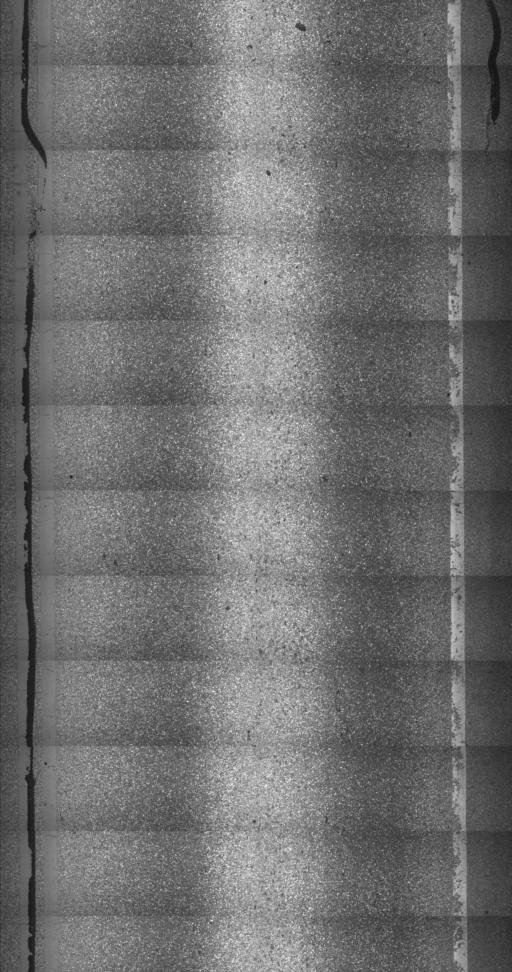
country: US
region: Vermont
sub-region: Chittenden County
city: Milton
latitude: 44.6704
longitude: -73.0149
